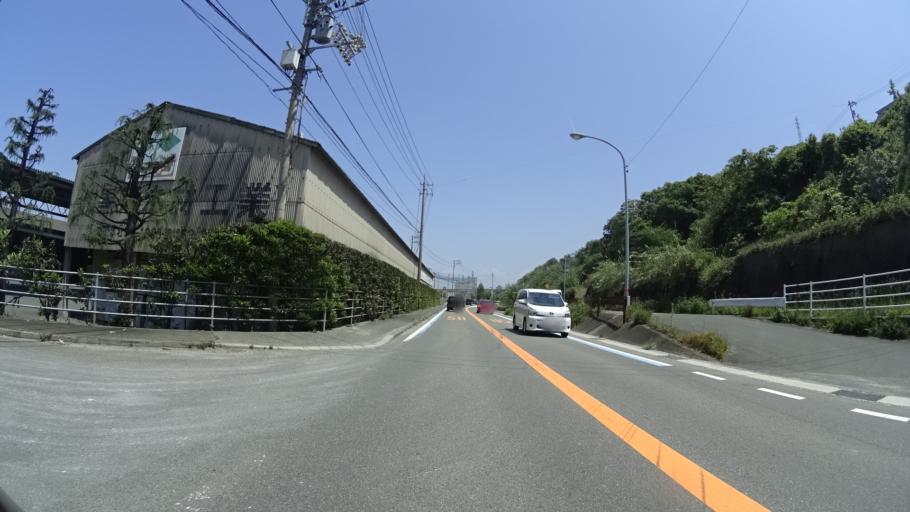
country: JP
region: Ehime
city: Ozu
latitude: 33.6187
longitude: 132.4956
